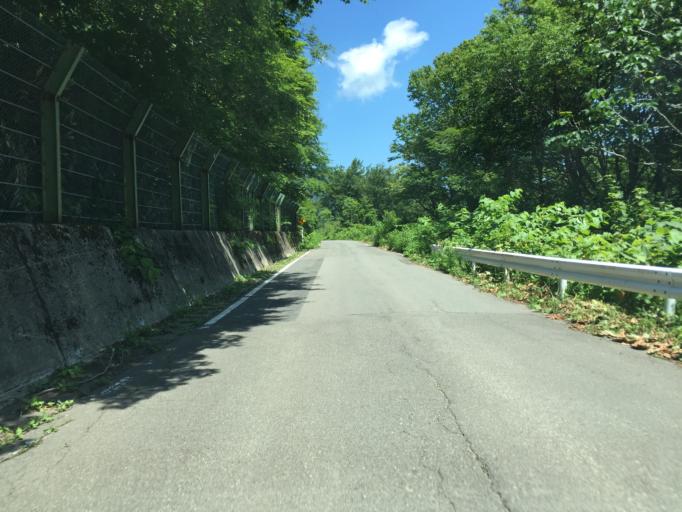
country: JP
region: Fukushima
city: Nihommatsu
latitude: 37.6676
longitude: 140.2706
